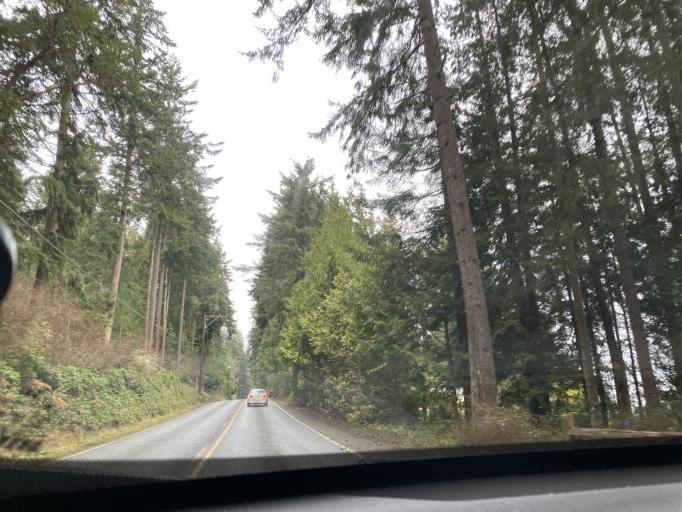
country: US
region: Washington
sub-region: Island County
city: Langley
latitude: 48.0645
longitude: -122.4590
